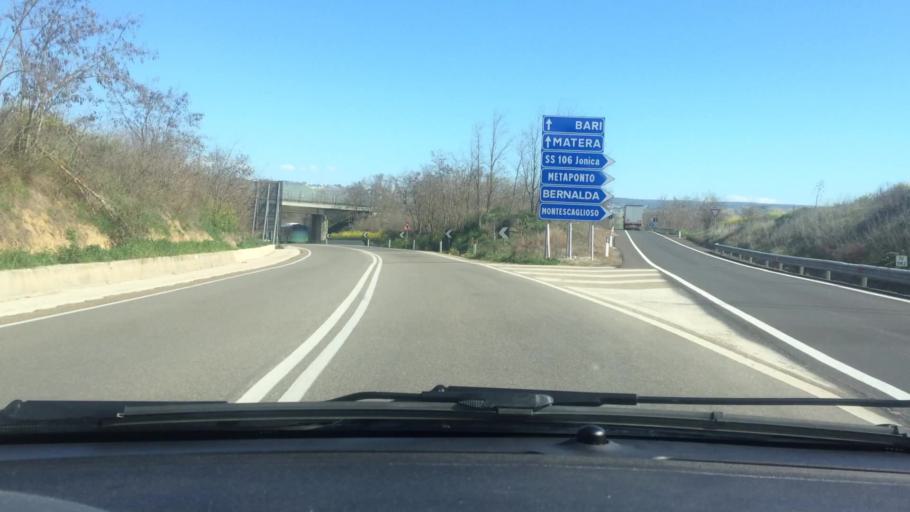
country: IT
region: Basilicate
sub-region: Provincia di Matera
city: Miglionico
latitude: 40.5951
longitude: 16.5649
